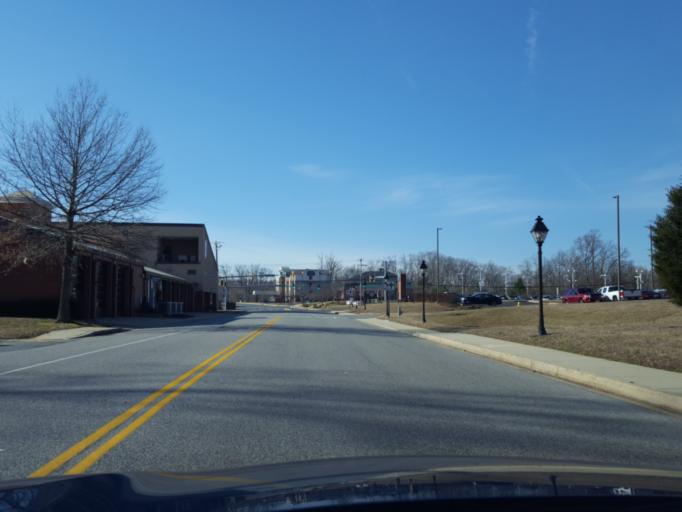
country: US
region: Maryland
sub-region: Calvert County
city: Prince Frederick
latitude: 38.5351
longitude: -76.5826
